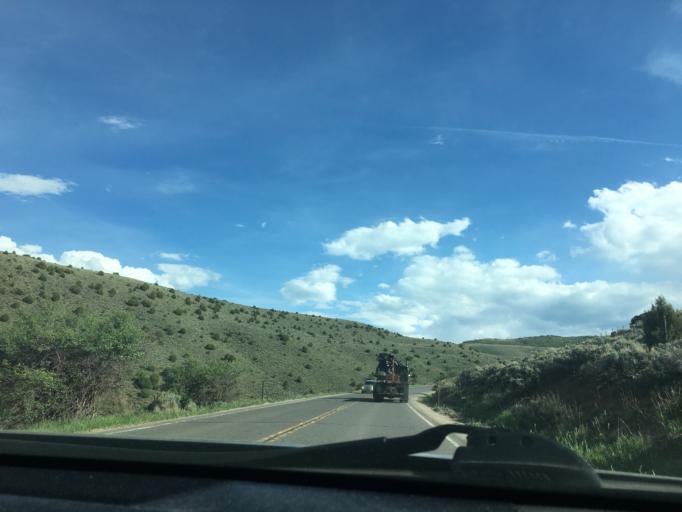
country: US
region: Colorado
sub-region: Eagle County
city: Edwards
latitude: 39.8331
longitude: -106.6383
